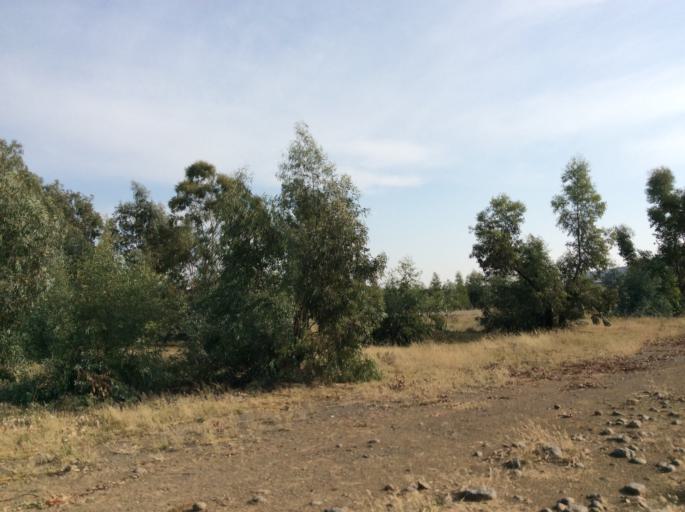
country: LS
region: Mafeteng
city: Mafeteng
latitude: -29.7243
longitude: 27.0246
